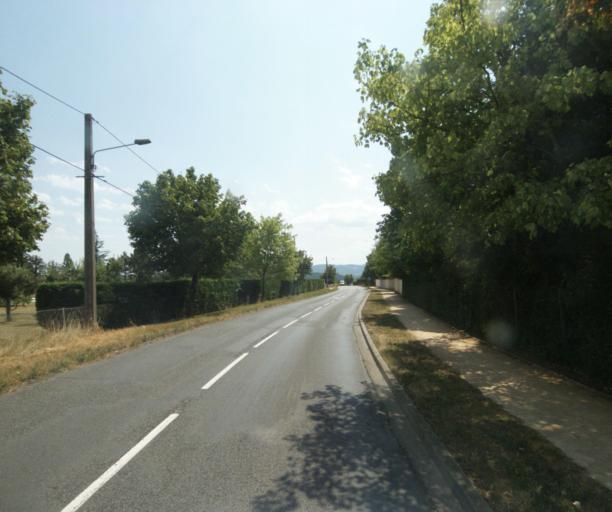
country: FR
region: Rhone-Alpes
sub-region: Departement du Rhone
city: Saint-Germain-Nuelles
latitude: 45.8477
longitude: 4.6117
